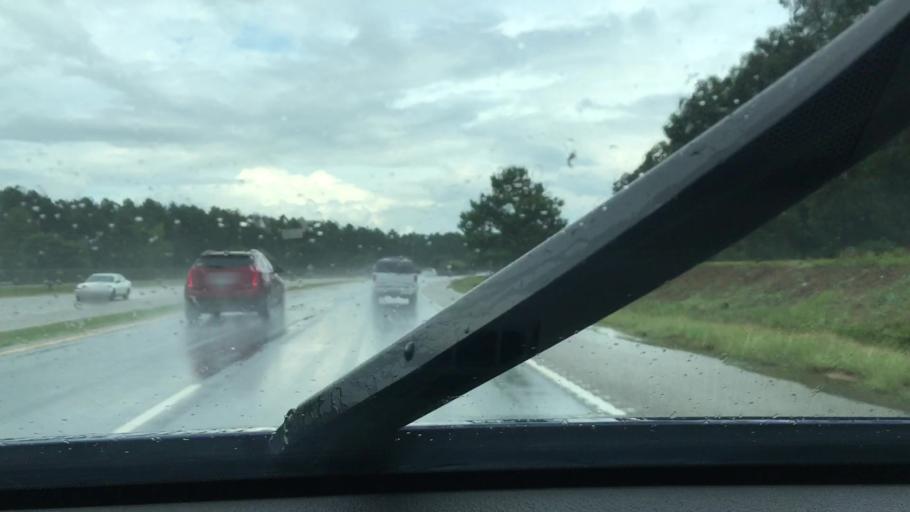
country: US
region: South Carolina
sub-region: Sumter County
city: Cherryvale
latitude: 33.9630
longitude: -80.4644
